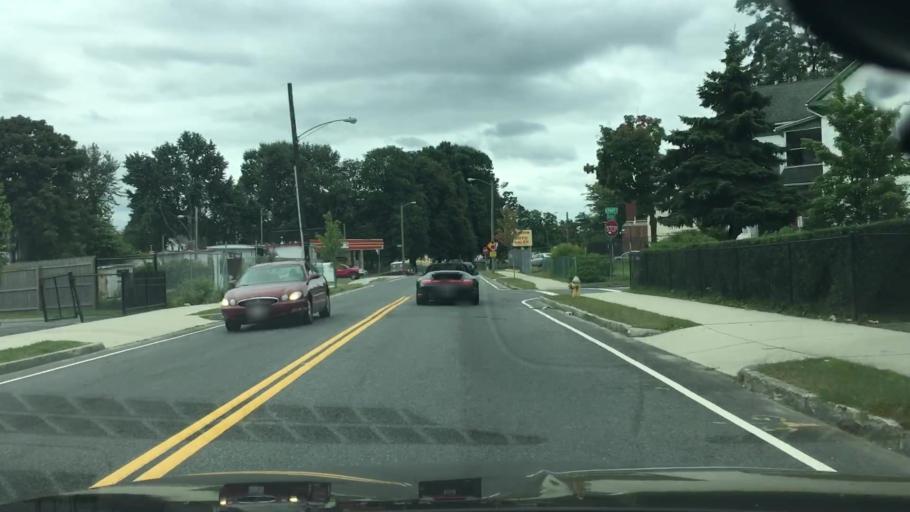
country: US
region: Massachusetts
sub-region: Hampden County
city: Springfield
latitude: 42.1120
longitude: -72.5770
